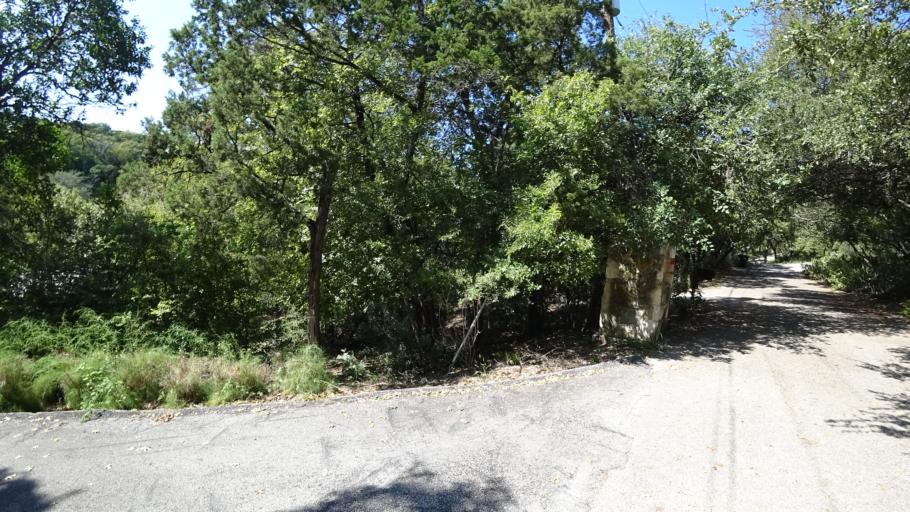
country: US
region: Texas
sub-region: Travis County
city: West Lake Hills
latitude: 30.3068
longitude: -97.7972
